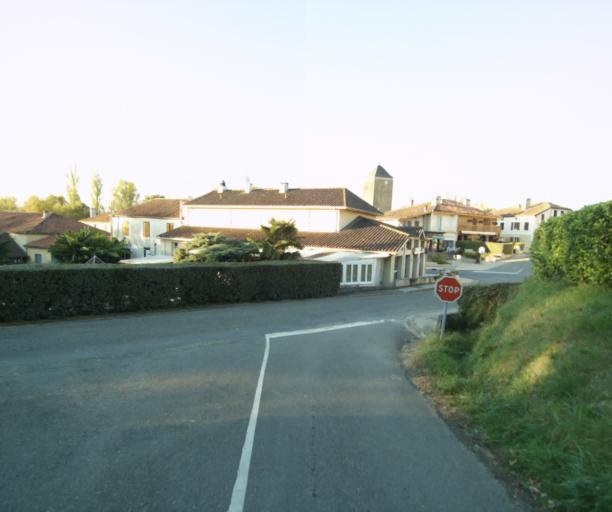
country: FR
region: Midi-Pyrenees
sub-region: Departement du Gers
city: Eauze
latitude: 43.7649
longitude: 0.1667
